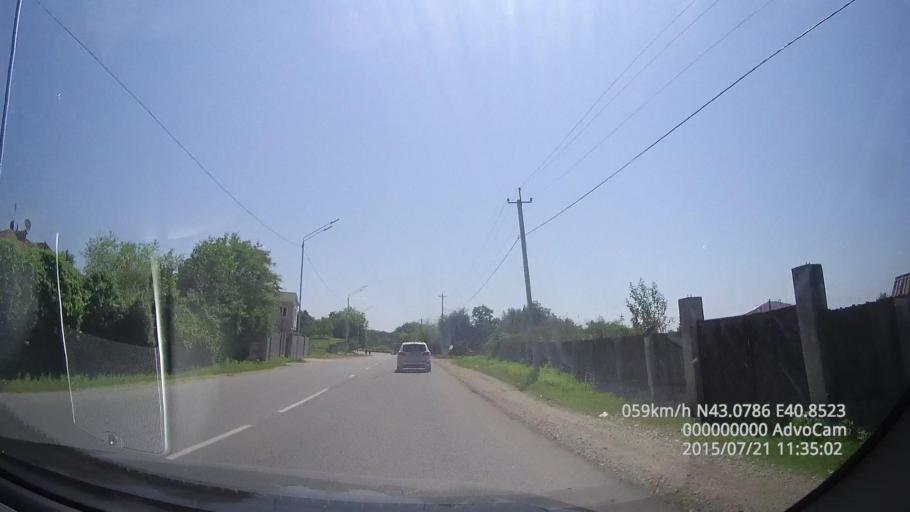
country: GE
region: Abkhazia
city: Stantsiya Novyy Afon
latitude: 43.0785
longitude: 40.8530
